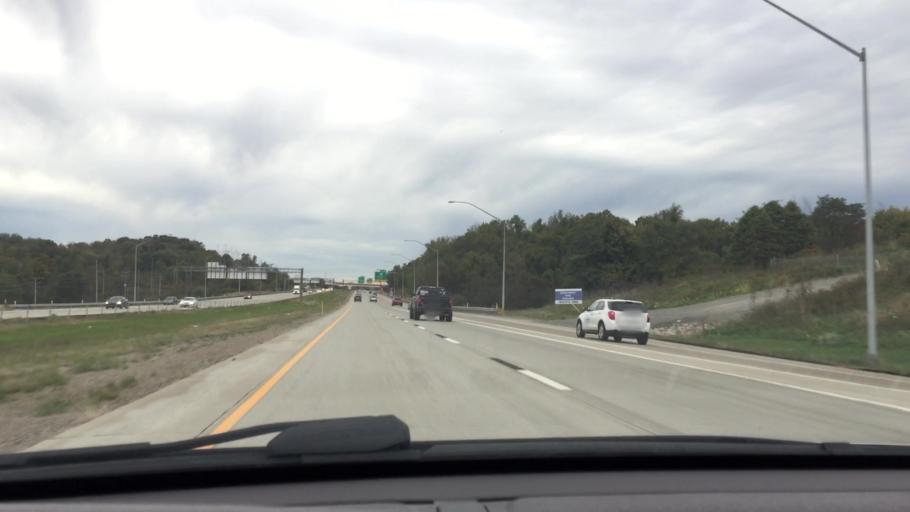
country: US
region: Pennsylvania
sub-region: Allegheny County
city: Imperial
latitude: 40.4912
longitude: -80.2719
